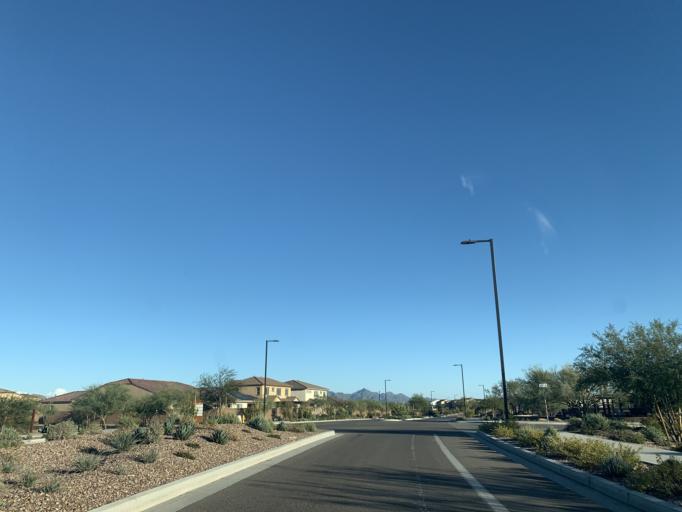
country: US
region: Arizona
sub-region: Maricopa County
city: Cave Creek
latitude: 33.6888
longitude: -112.0148
